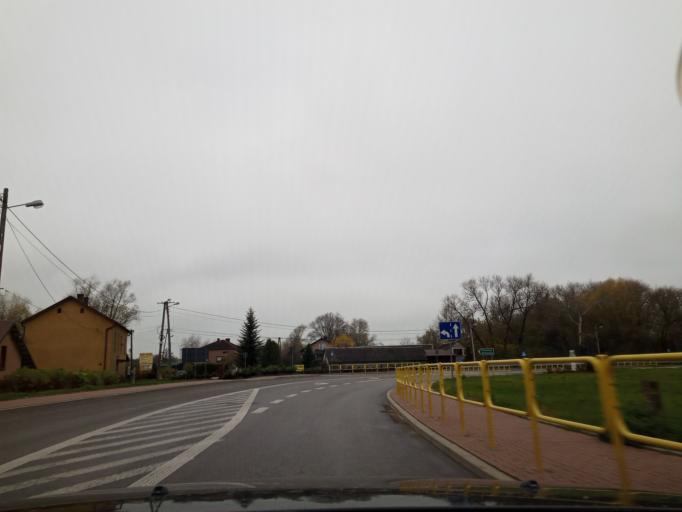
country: PL
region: Swietokrzyskie
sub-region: Powiat pinczowski
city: Dzialoszyce
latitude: 50.3584
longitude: 20.3516
